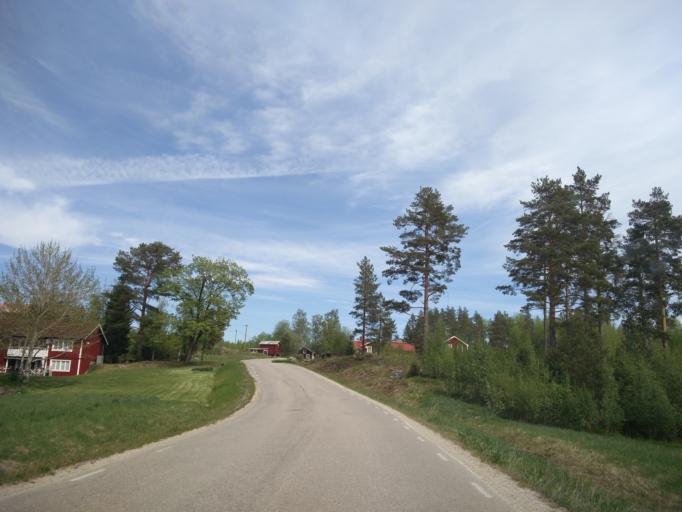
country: SE
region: Gaevleborg
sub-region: Hudiksvalls Kommun
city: Sorforsa
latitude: 61.7000
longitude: 16.9330
